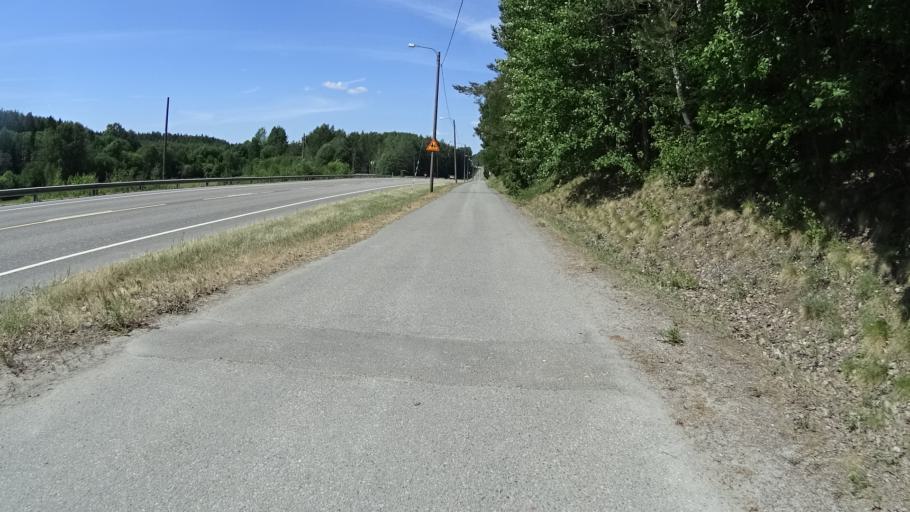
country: FI
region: Uusimaa
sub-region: Raaseporin
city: Karis
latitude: 60.0957
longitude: 23.6132
